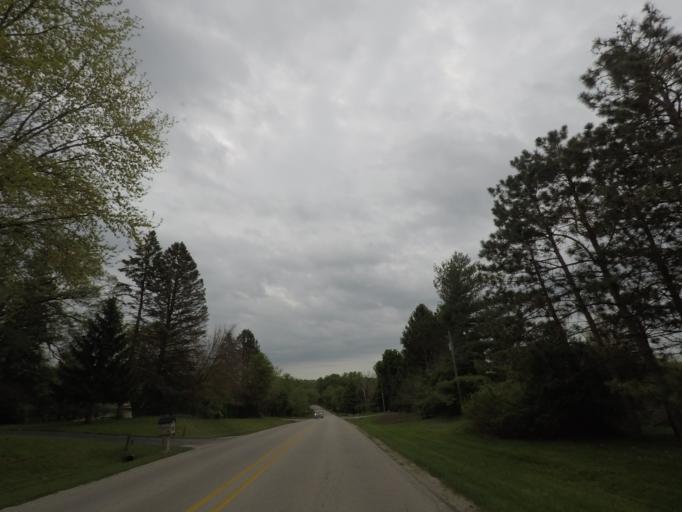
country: US
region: Illinois
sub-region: Winnebago County
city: Roscoe
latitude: 42.4370
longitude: -88.9850
